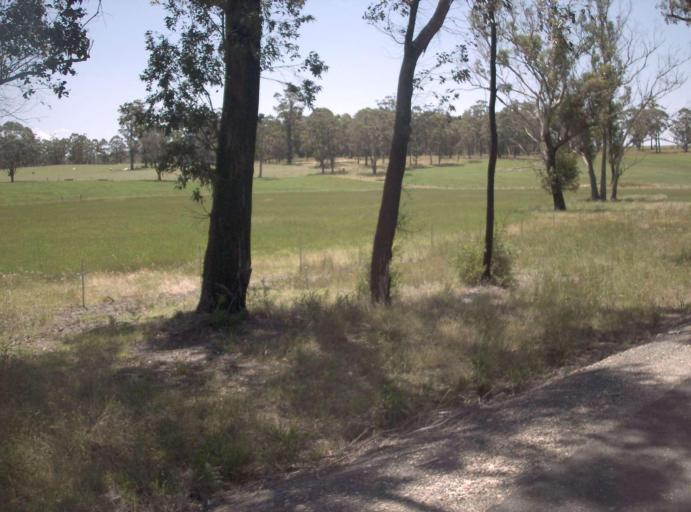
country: AU
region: Victoria
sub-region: East Gippsland
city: Lakes Entrance
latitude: -37.7547
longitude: 148.2783
